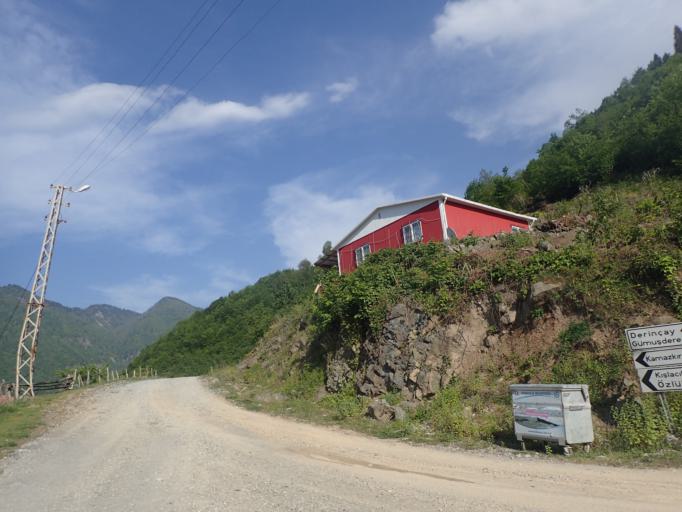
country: TR
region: Ordu
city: Topcam
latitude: 40.7028
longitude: 37.8450
